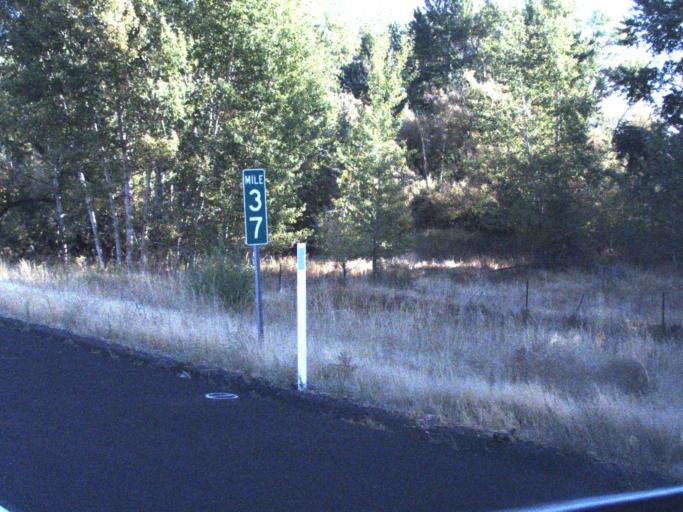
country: US
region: Washington
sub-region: Yakima County
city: Union Gap
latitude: 46.5533
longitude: -120.4703
